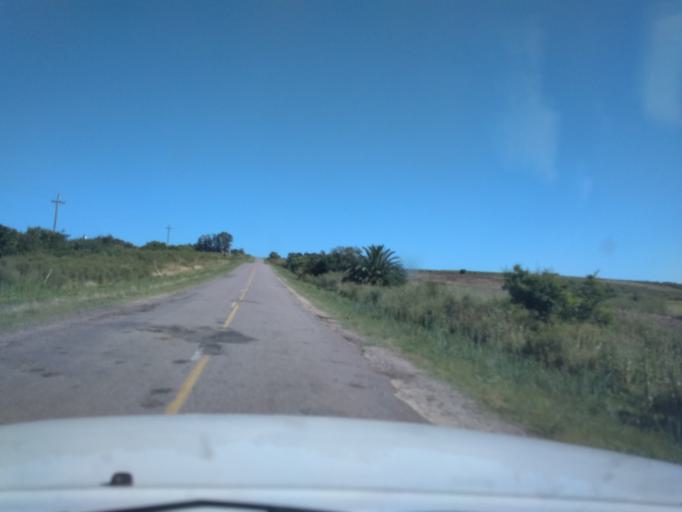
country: UY
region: Canelones
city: San Ramon
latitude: -34.1717
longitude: -55.9443
